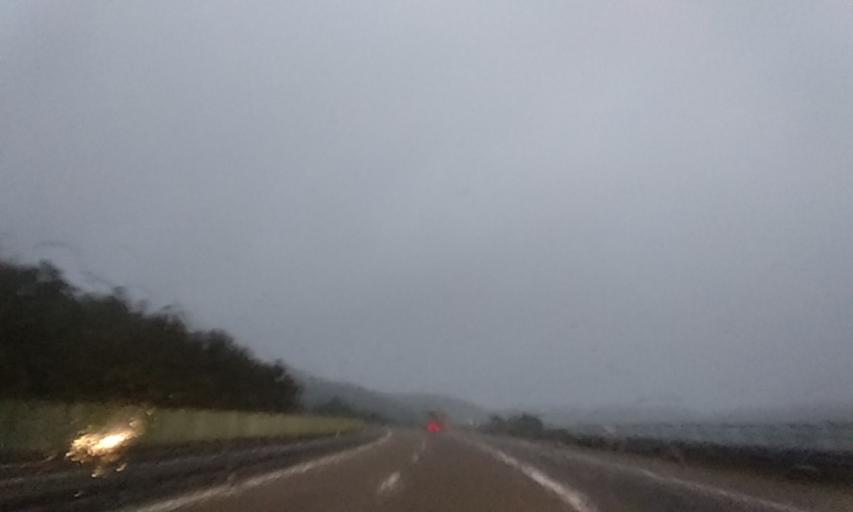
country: PT
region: Viana do Castelo
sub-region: Ponte de Lima
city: Ponte de Lima
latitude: 41.8392
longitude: -8.6024
